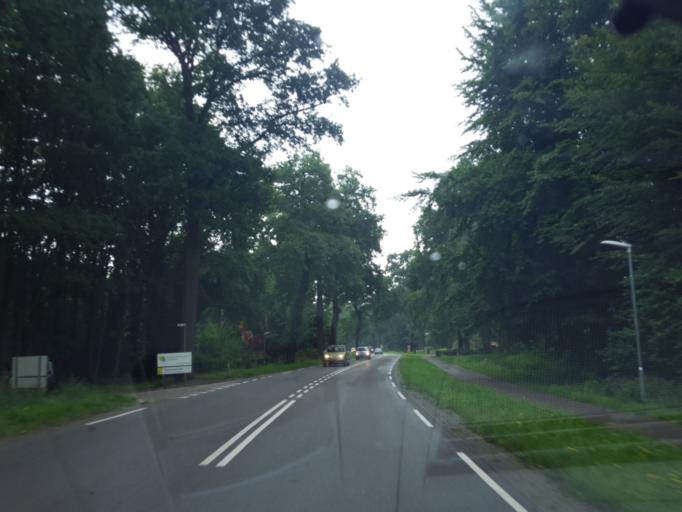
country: NL
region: Limburg
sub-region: Gemeente Venray
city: Venray
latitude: 51.4704
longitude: 6.0573
